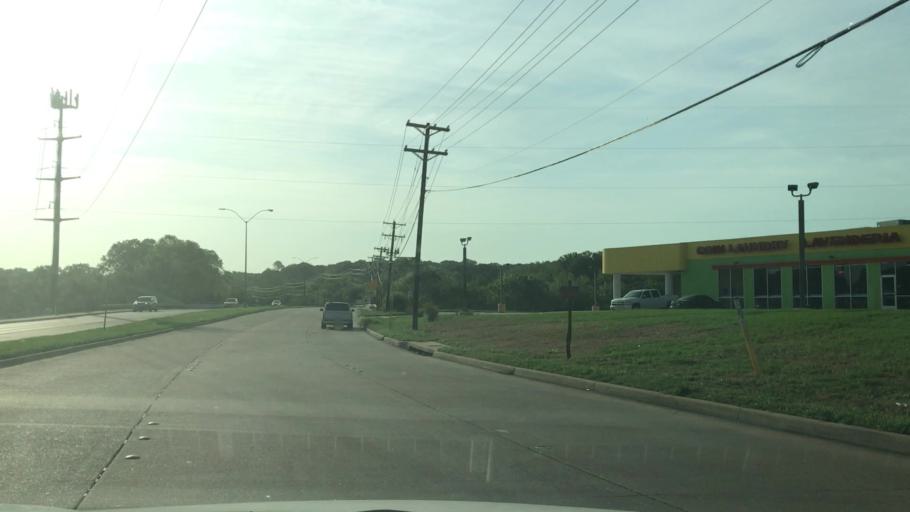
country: US
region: Texas
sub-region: Tarrant County
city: Pantego
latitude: 32.7575
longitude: -97.1562
